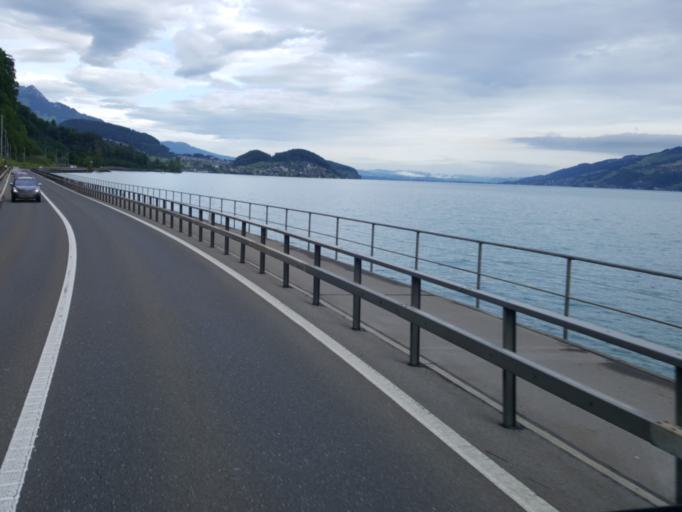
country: CH
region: Bern
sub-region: Frutigen-Niedersimmental District
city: Aeschi
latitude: 46.6623
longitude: 7.7416
